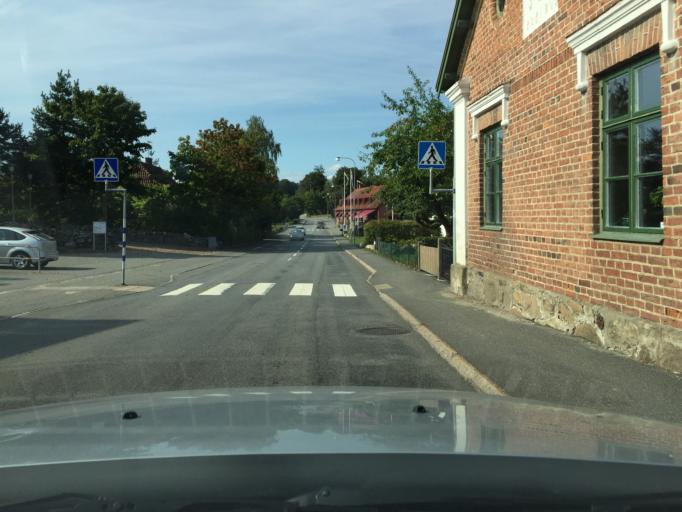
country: SE
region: Skane
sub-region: Kristianstads Kommun
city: Degeberga
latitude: 55.7248
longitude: 14.1054
